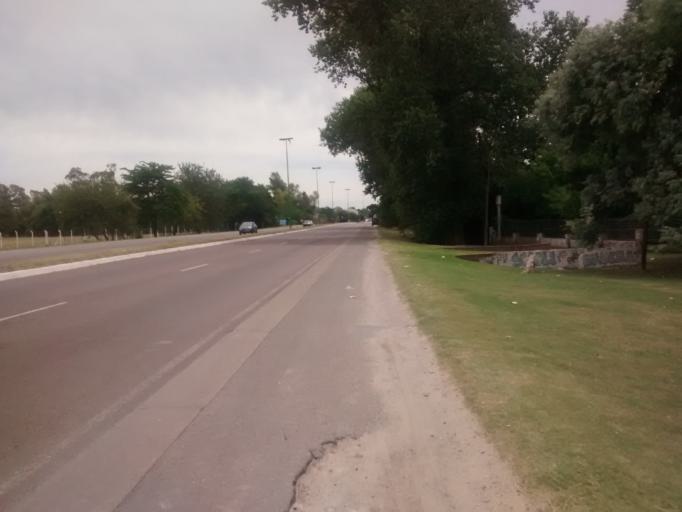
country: AR
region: Buenos Aires
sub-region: Partido de La Plata
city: La Plata
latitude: -34.8590
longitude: -58.0688
